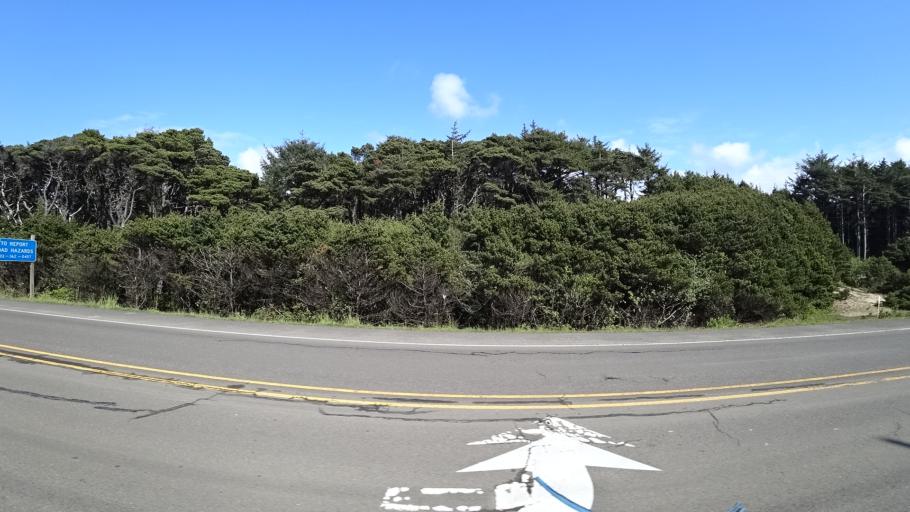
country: US
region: Oregon
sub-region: Lincoln County
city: Newport
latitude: 44.5492
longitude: -124.0726
